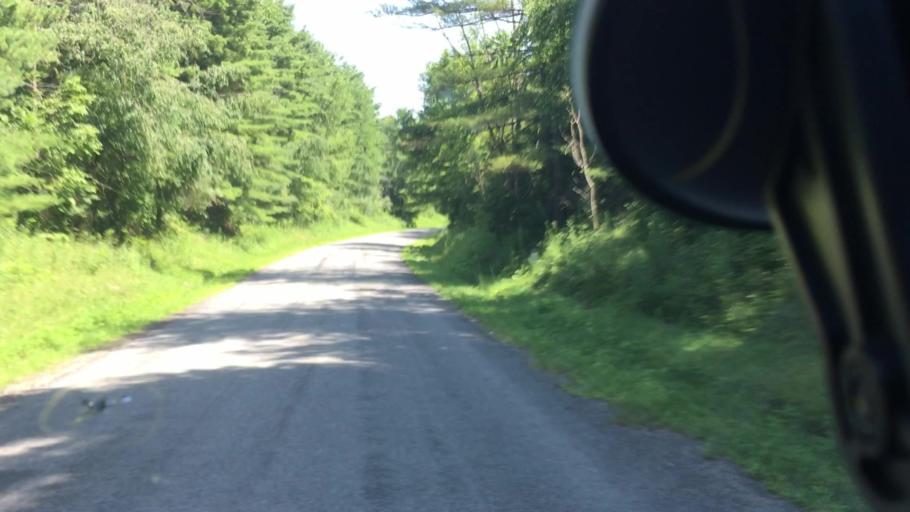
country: US
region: Ohio
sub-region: Columbiana County
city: Lisbon
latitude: 40.7661
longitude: -80.7922
